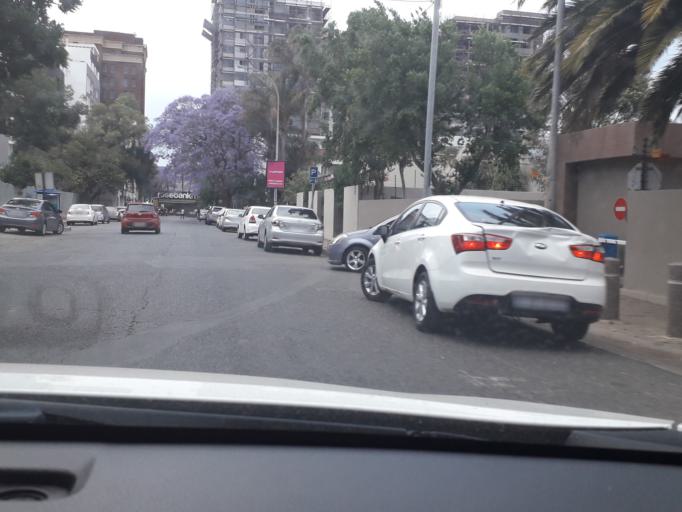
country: ZA
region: Gauteng
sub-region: City of Johannesburg Metropolitan Municipality
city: Johannesburg
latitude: -26.1439
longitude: 28.0401
